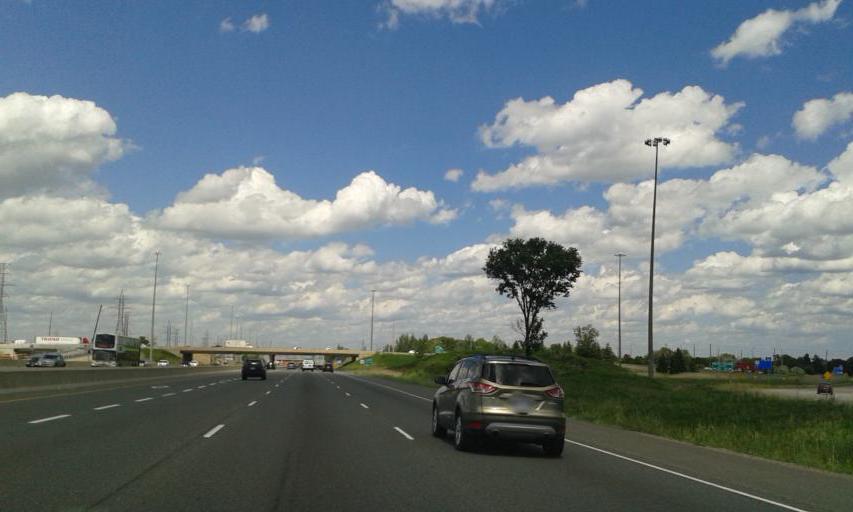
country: CA
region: Ontario
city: Mississauga
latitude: 43.5402
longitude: -79.7130
